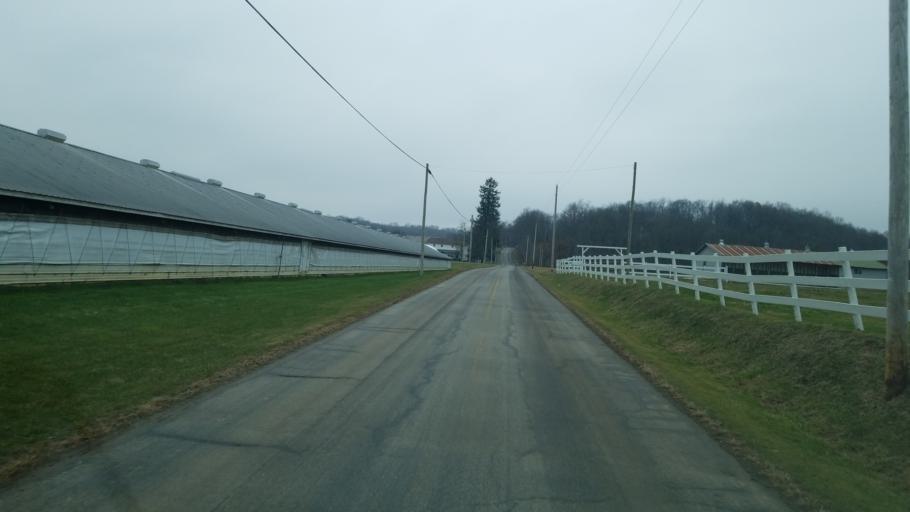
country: US
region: Ohio
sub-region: Holmes County
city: Millersburg
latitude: 40.4847
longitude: -81.8597
